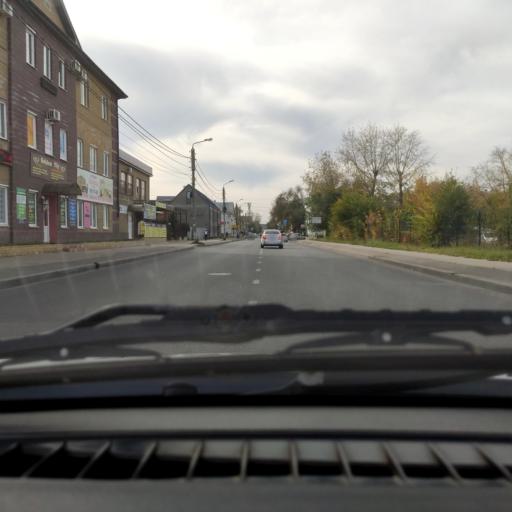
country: RU
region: Samara
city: Tol'yatti
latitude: 53.5172
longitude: 49.4101
